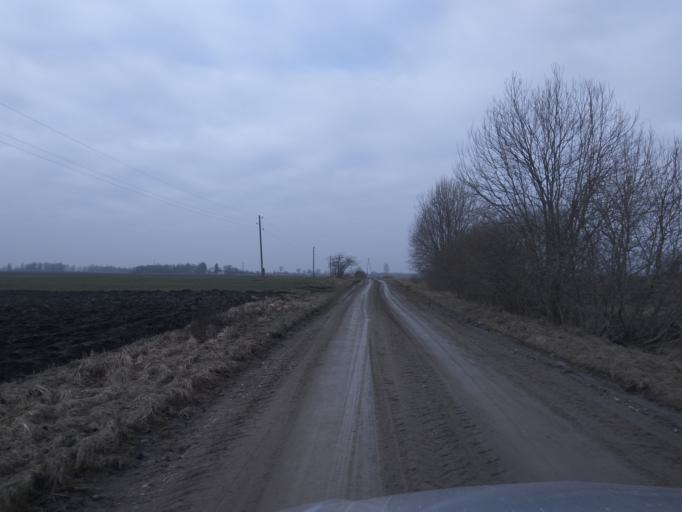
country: LV
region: Durbe
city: Liegi
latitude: 56.6680
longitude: 21.3775
